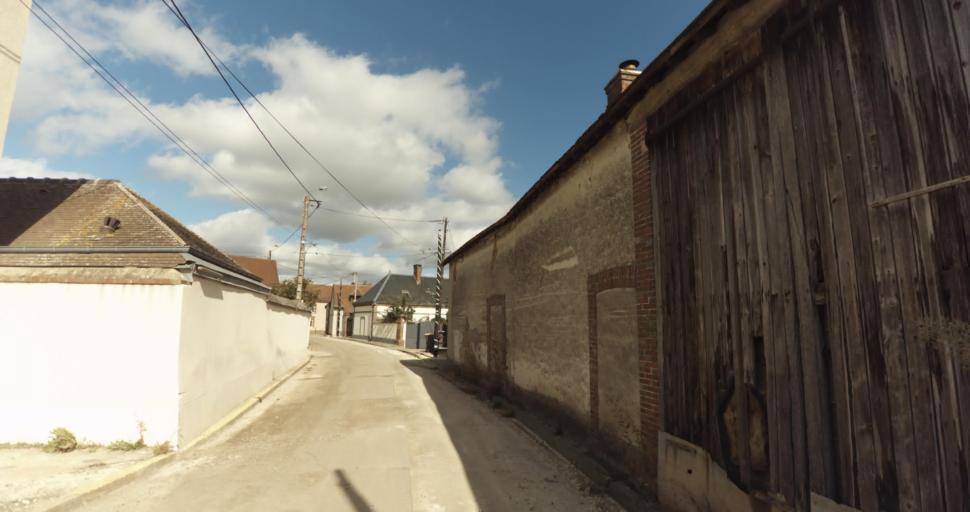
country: FR
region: Centre
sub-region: Departement d'Eure-et-Loir
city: Garnay
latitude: 48.7268
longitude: 1.3278
